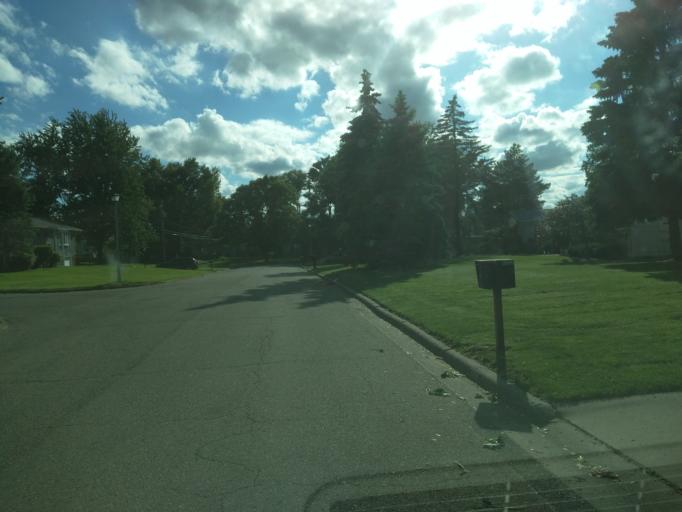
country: US
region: Michigan
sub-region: Eaton County
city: Waverly
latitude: 42.7514
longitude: -84.6157
